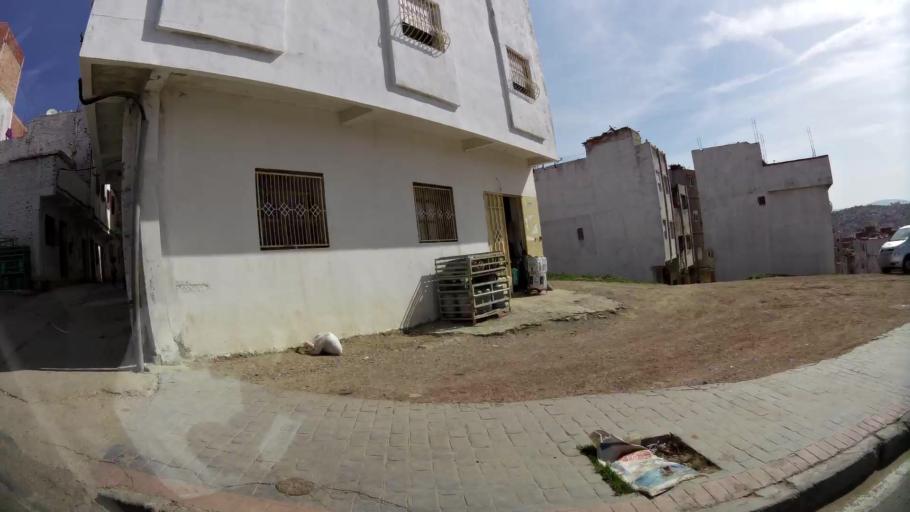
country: MA
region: Tanger-Tetouan
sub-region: Tanger-Assilah
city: Tangier
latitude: 35.7298
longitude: -5.8140
